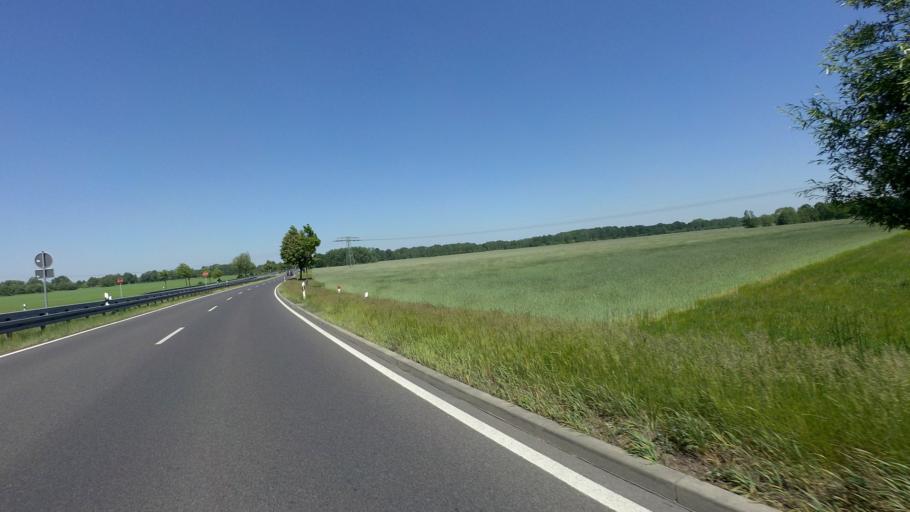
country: DE
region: Brandenburg
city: Peitz
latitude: 51.8190
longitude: 14.3865
